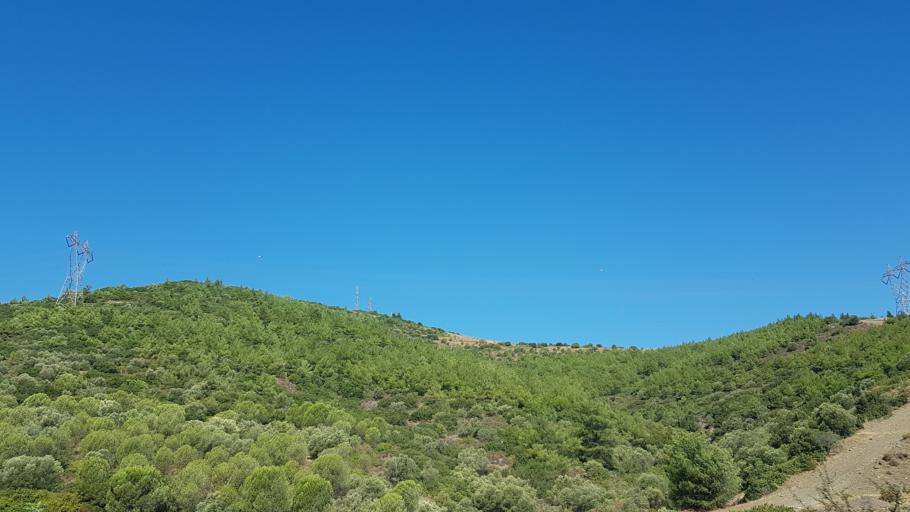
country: TR
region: Izmir
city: Buca
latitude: 38.4048
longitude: 27.2320
